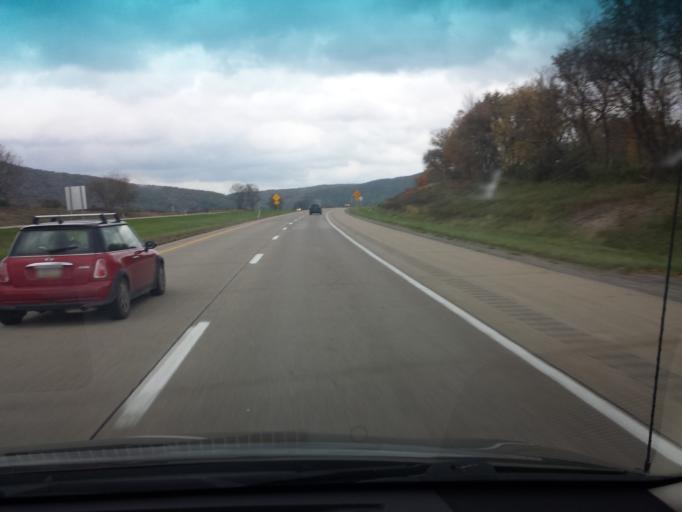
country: US
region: Pennsylvania
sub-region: Centre County
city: Bellefonte
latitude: 40.9246
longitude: -77.7410
